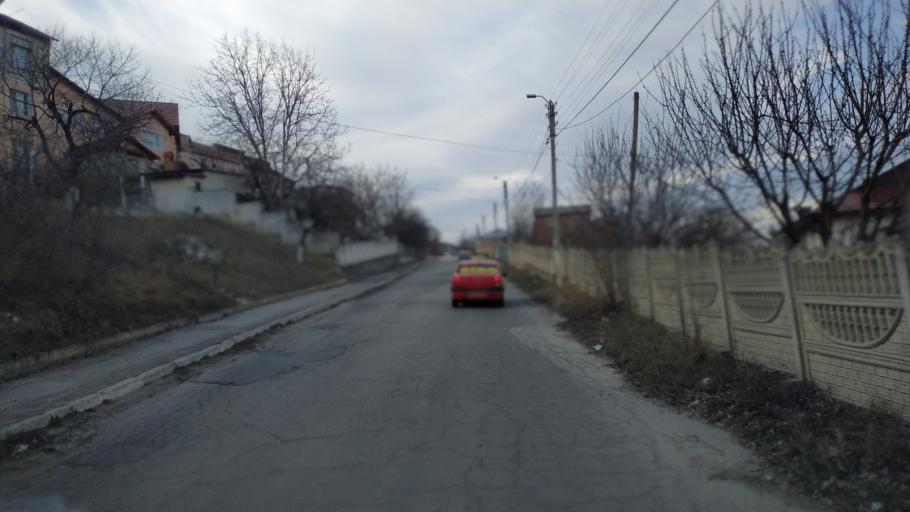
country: MD
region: Laloveni
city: Ialoveni
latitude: 46.9547
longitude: 28.7626
